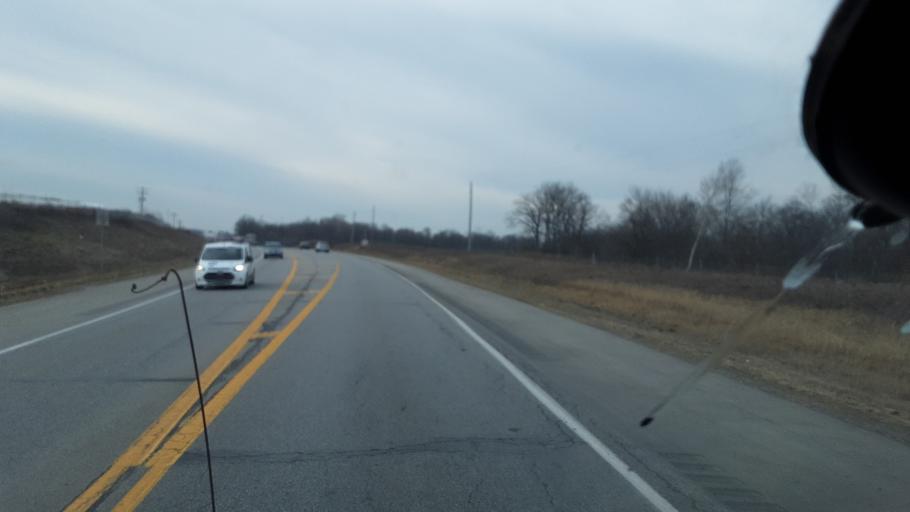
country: US
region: Indiana
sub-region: DeKalb County
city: Waterloo
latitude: 41.4399
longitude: -85.0412
